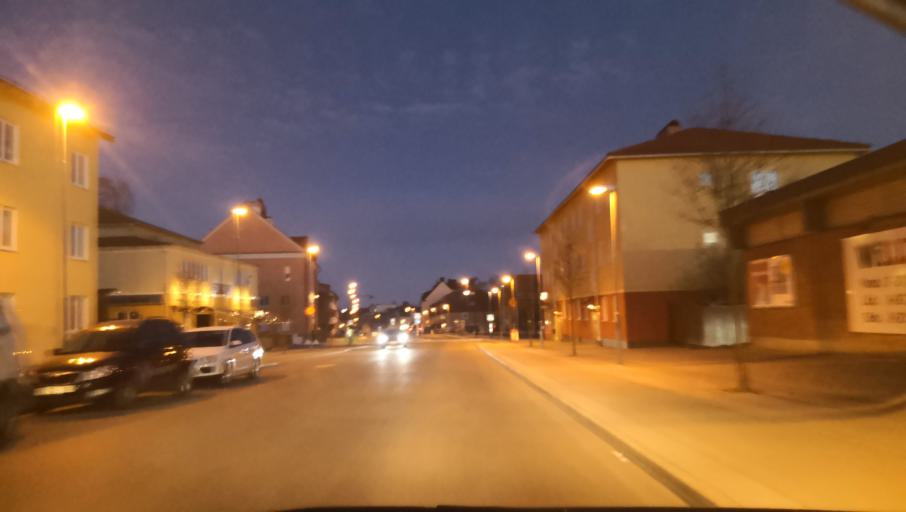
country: SE
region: Stockholm
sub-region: Nynashamns Kommun
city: Nynashamn
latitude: 58.9130
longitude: 17.9481
